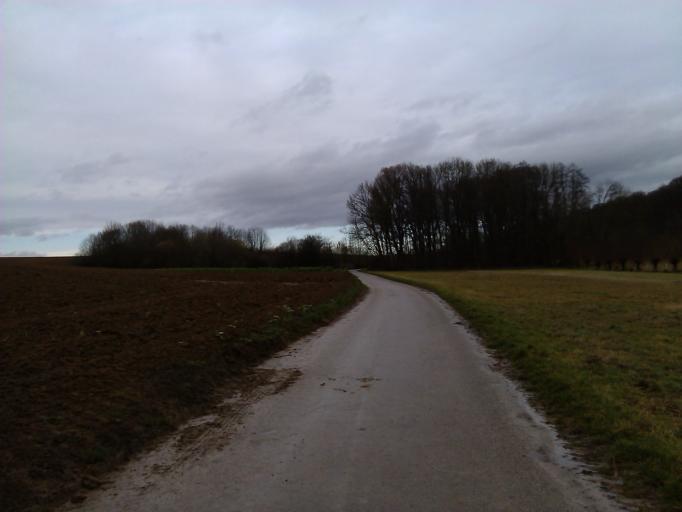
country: DE
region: Baden-Wuerttemberg
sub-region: Regierungsbezirk Stuttgart
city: Bad Wimpfen
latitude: 49.2026
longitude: 9.1584
